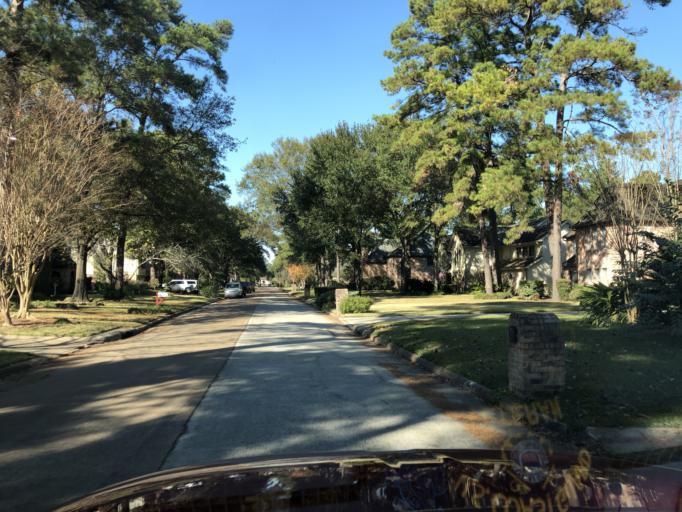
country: US
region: Texas
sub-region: Harris County
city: Tomball
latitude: 30.0214
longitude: -95.5410
